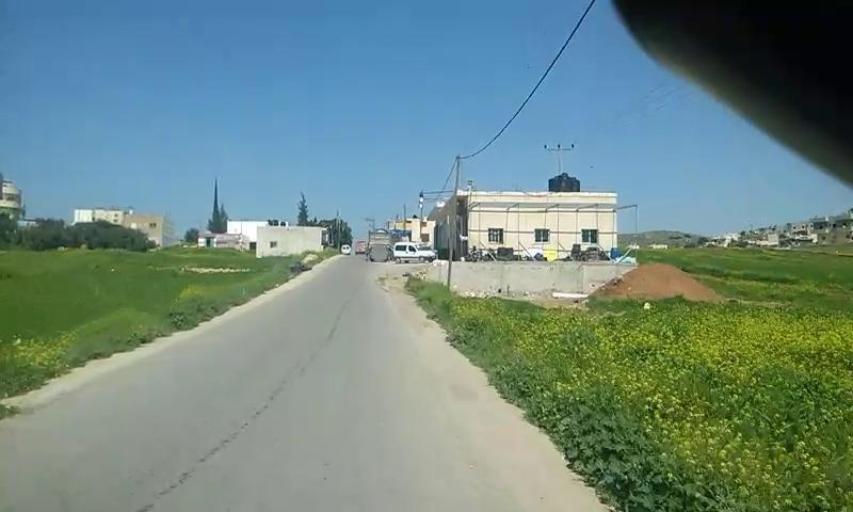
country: PS
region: West Bank
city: Al Majd
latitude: 31.4775
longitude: 34.9520
